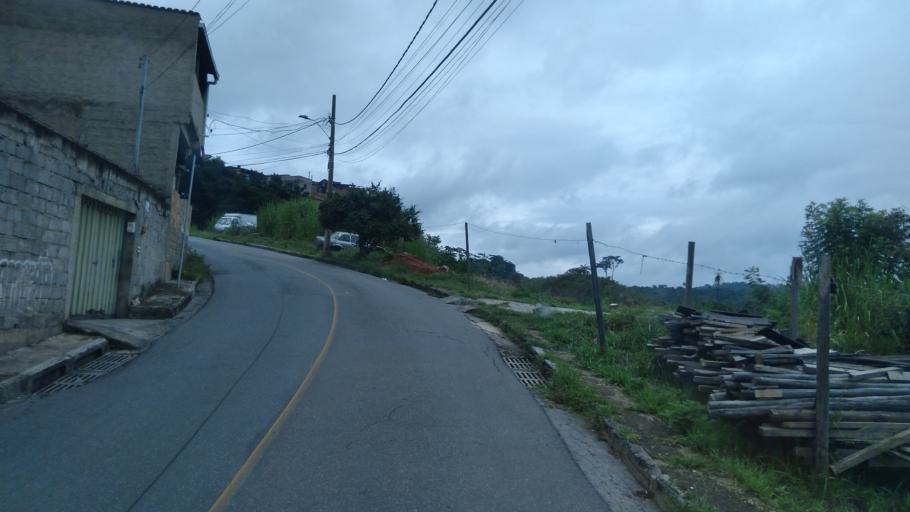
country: BR
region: Minas Gerais
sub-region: Santa Luzia
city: Santa Luzia
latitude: -19.8317
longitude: -43.8670
